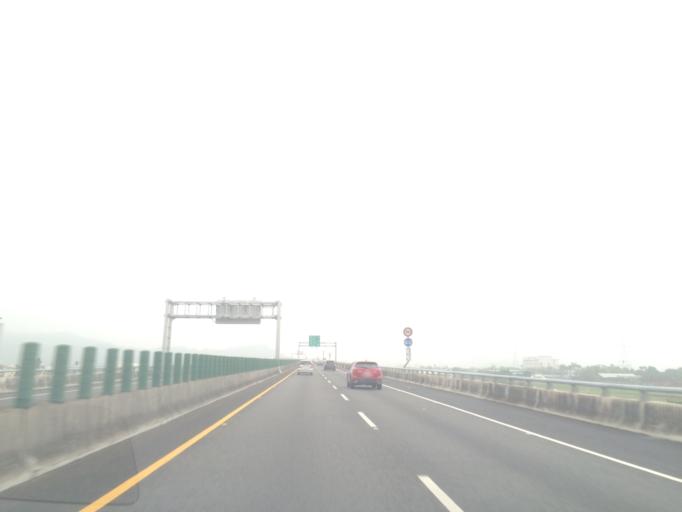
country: TW
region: Taiwan
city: Zhongxing New Village
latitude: 24.0238
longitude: 120.6755
